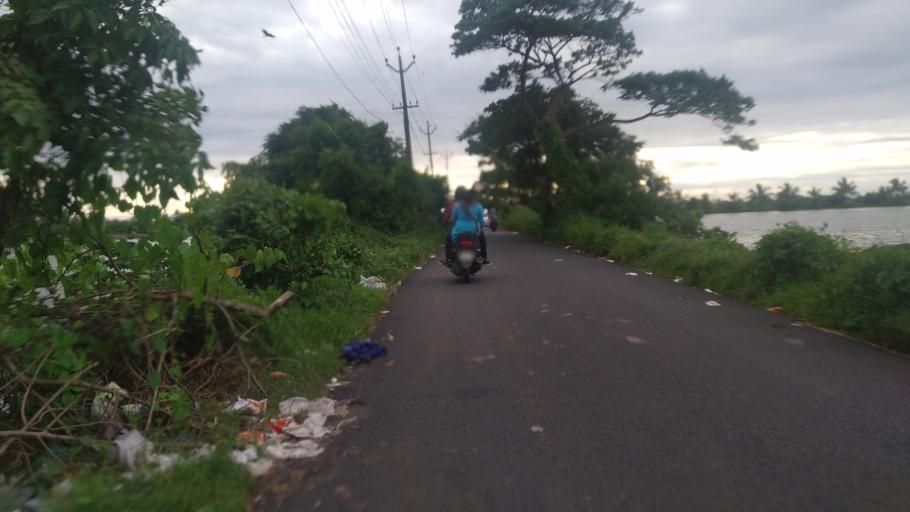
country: IN
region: Kerala
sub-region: Alappuzha
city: Arukutti
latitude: 9.8595
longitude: 76.2837
